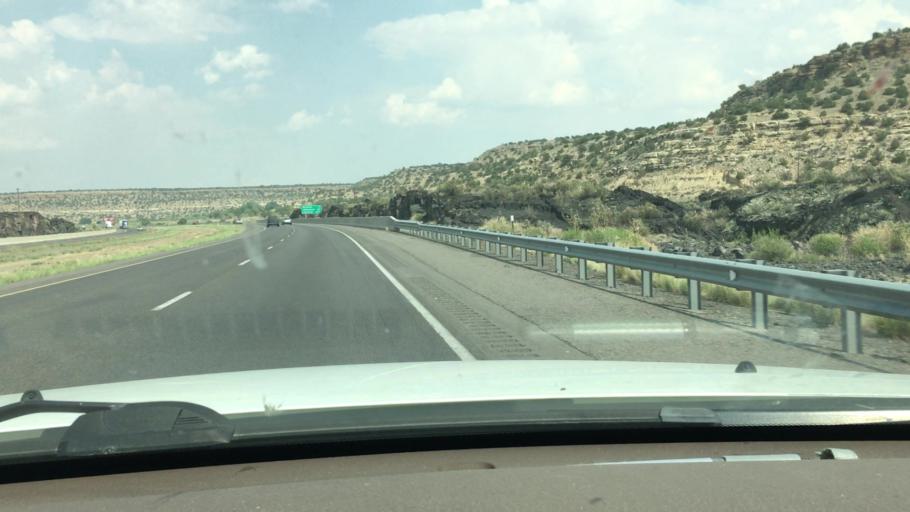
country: US
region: New Mexico
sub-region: Cibola County
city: Skyline-Ganipa
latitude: 35.0622
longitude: -107.7034
